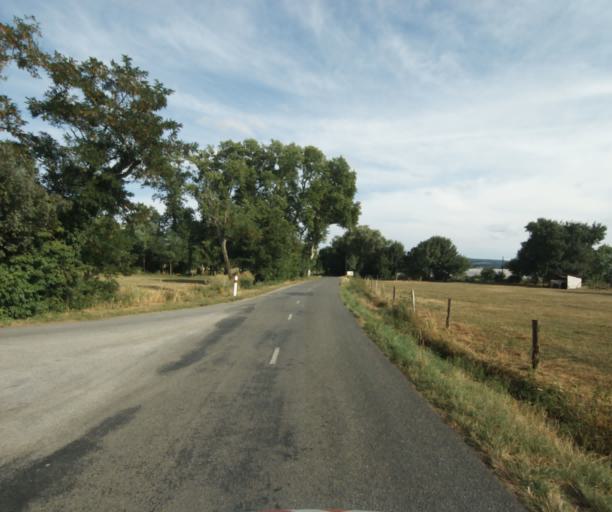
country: FR
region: Midi-Pyrenees
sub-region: Departement de la Haute-Garonne
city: Revel
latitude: 43.4846
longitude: 1.9859
